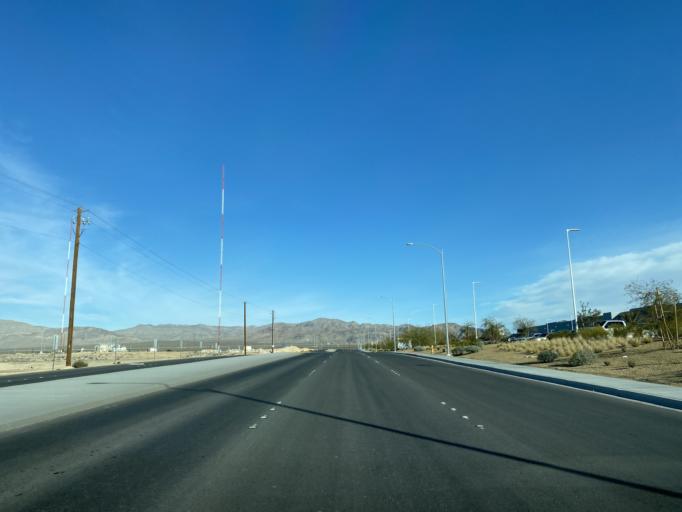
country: US
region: Nevada
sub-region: Clark County
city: Nellis Air Force Base
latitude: 36.2649
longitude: -115.0432
